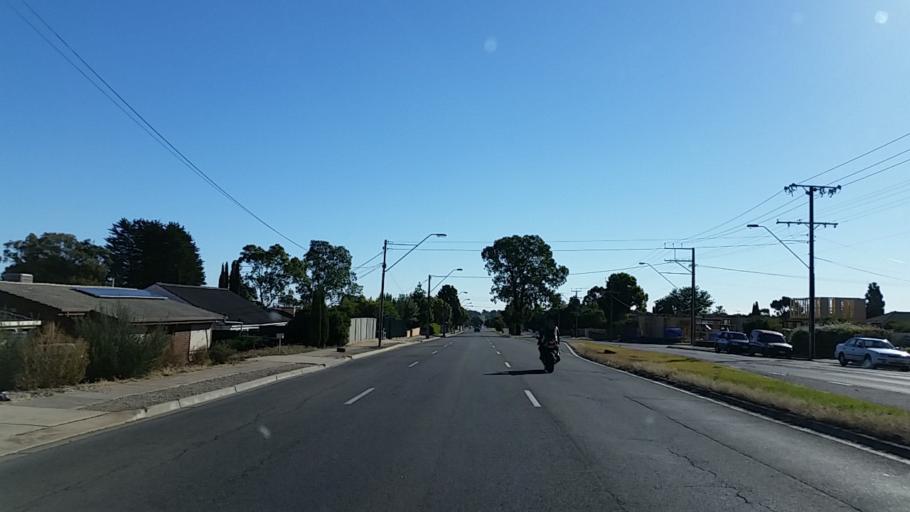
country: AU
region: South Australia
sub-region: Tea Tree Gully
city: Hope Valley
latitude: -34.8274
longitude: 138.7006
